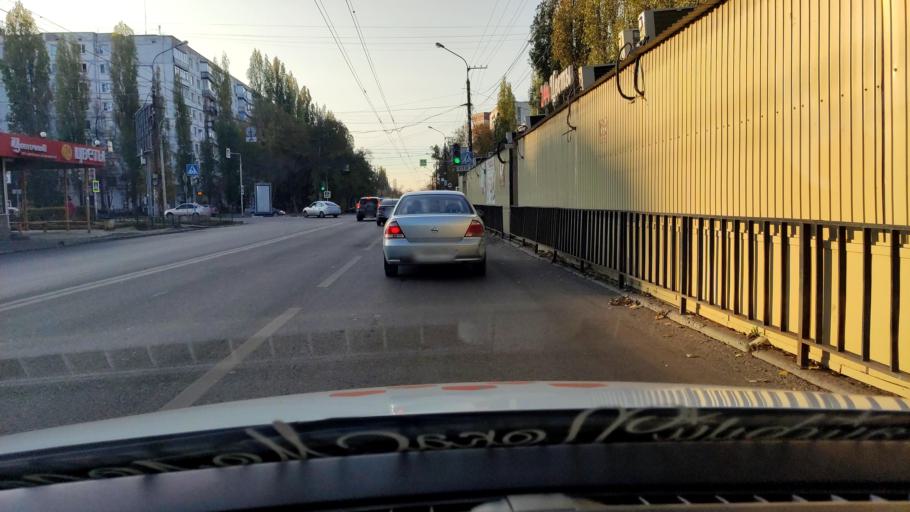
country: RU
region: Voronezj
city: Voronezh
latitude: 51.7073
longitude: 39.1741
